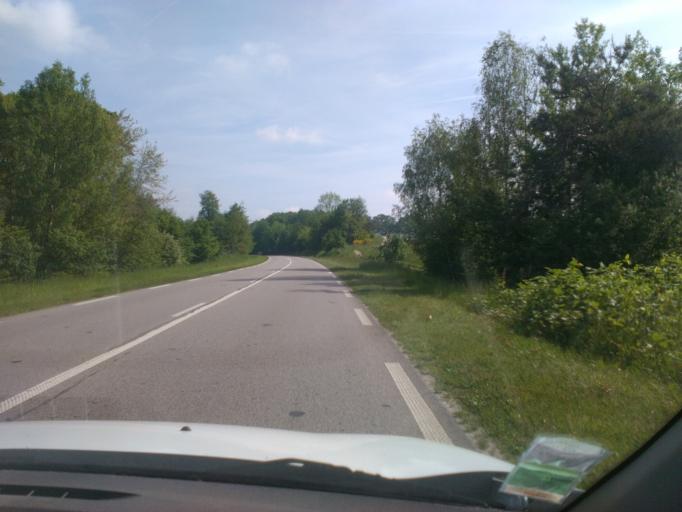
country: FR
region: Lorraine
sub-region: Departement des Vosges
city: Golbey
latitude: 48.2003
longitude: 6.4152
